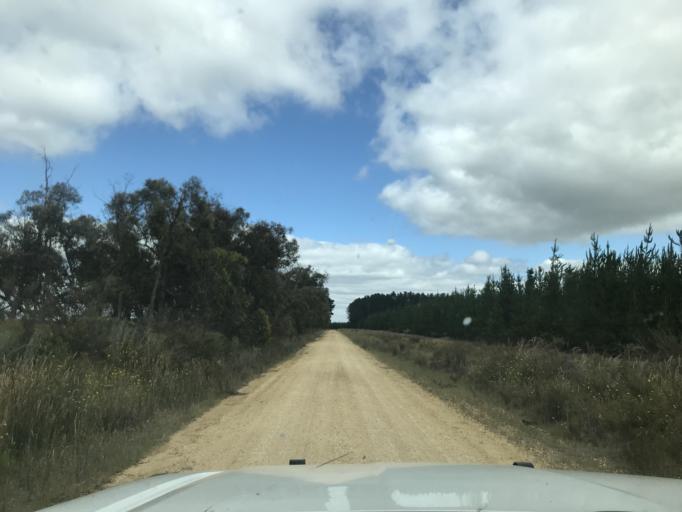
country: AU
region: South Australia
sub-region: Wattle Range
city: Penola
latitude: -37.3171
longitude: 141.1346
